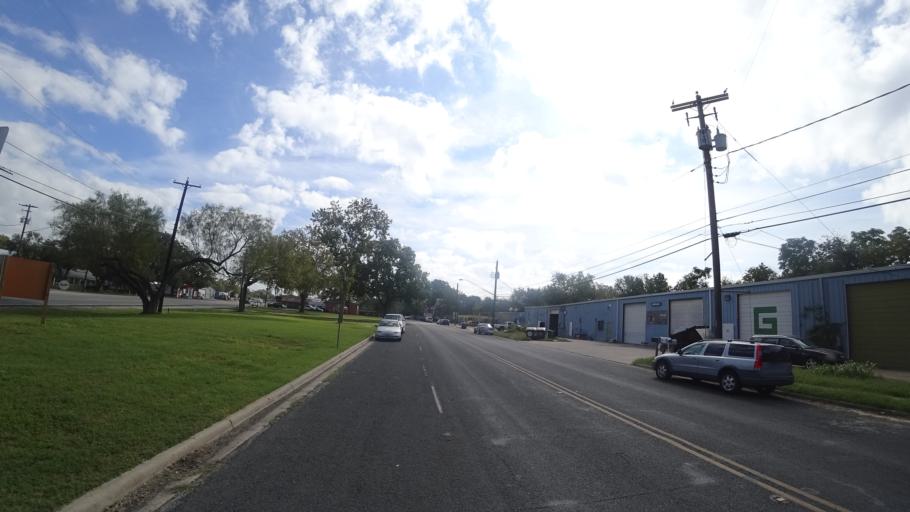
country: US
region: Texas
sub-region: Travis County
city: Austin
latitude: 30.2516
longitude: -97.7039
